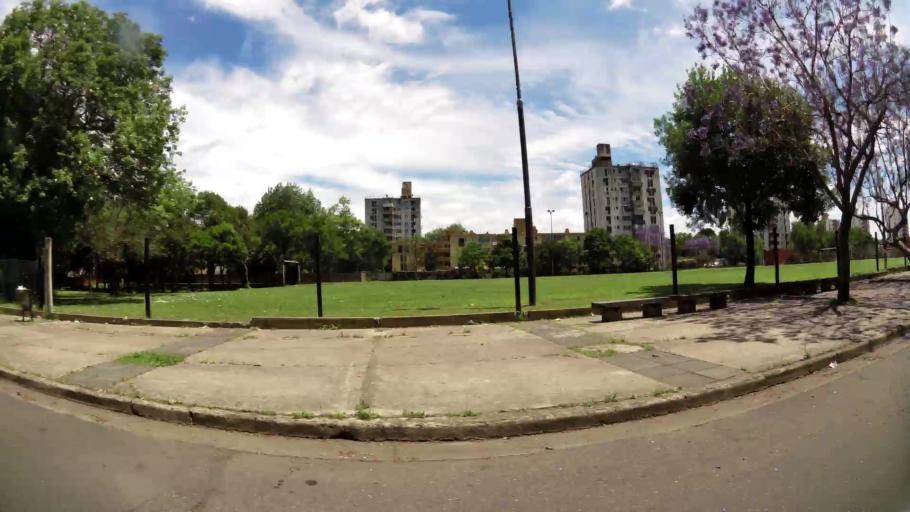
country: AR
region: Santa Fe
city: Gobernador Galvez
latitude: -32.9950
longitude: -60.6253
